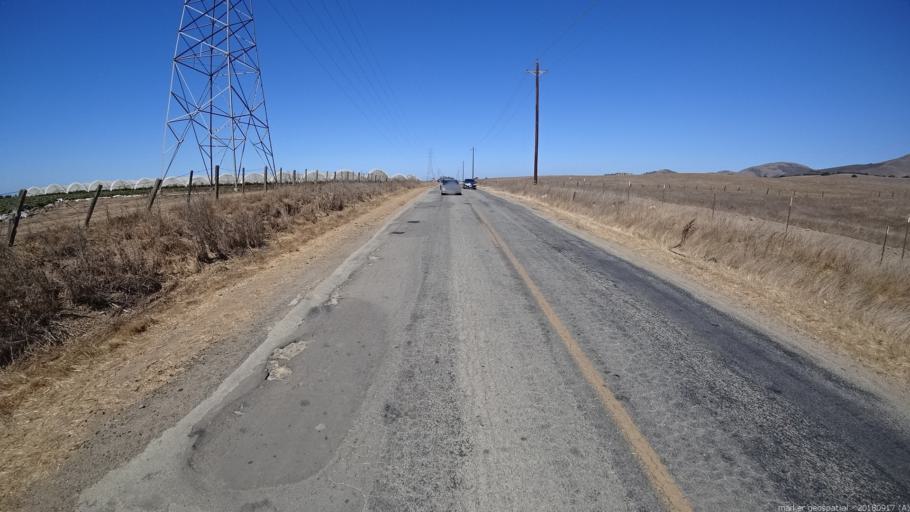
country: US
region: California
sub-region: Monterey County
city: Salinas
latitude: 36.7127
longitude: -121.5873
